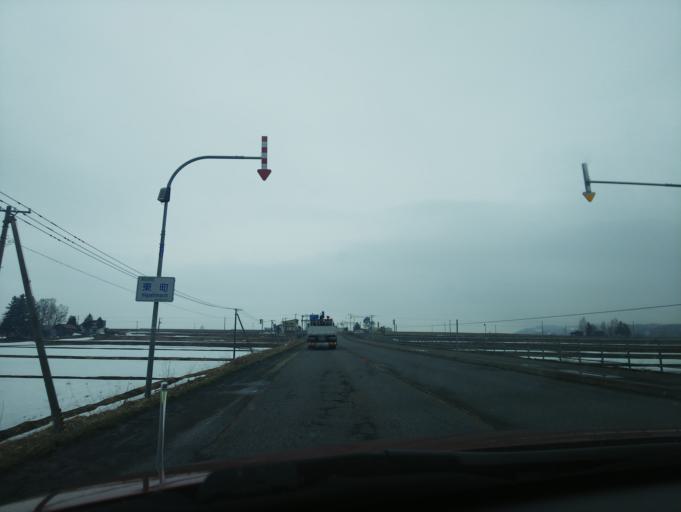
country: JP
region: Hokkaido
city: Nayoro
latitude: 44.0683
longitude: 142.3963
